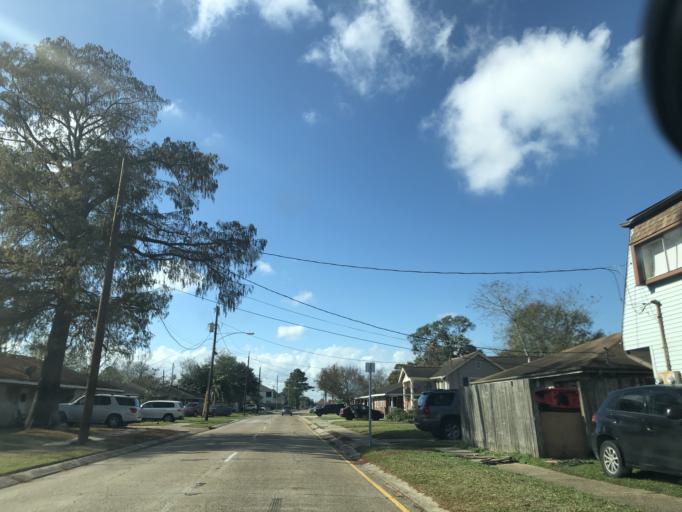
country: US
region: Louisiana
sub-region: Jefferson Parish
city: Metairie Terrace
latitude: 29.9815
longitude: -90.1616
